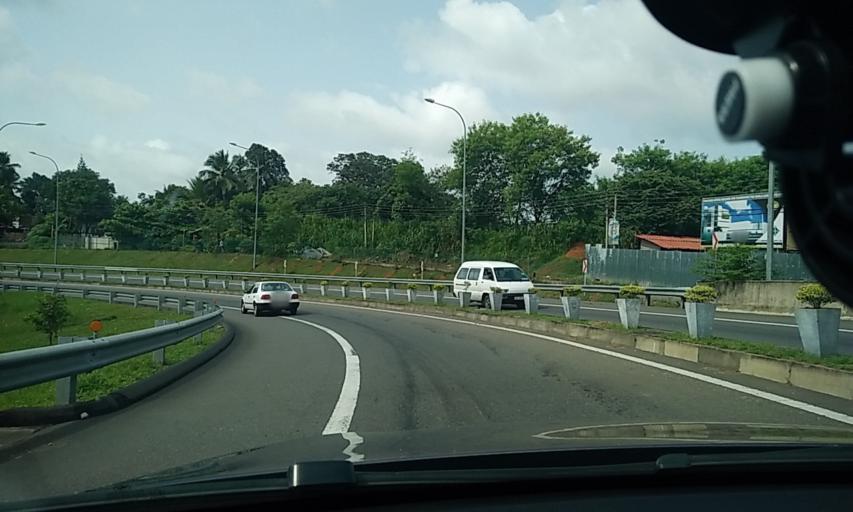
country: LK
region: Western
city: Homagama
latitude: 6.8406
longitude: 79.9793
